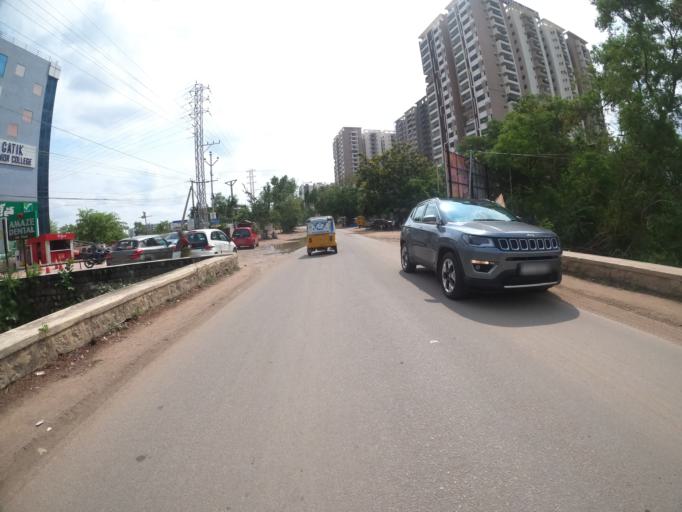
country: IN
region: Telangana
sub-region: Medak
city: Serilingampalle
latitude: 17.3880
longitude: 78.3427
